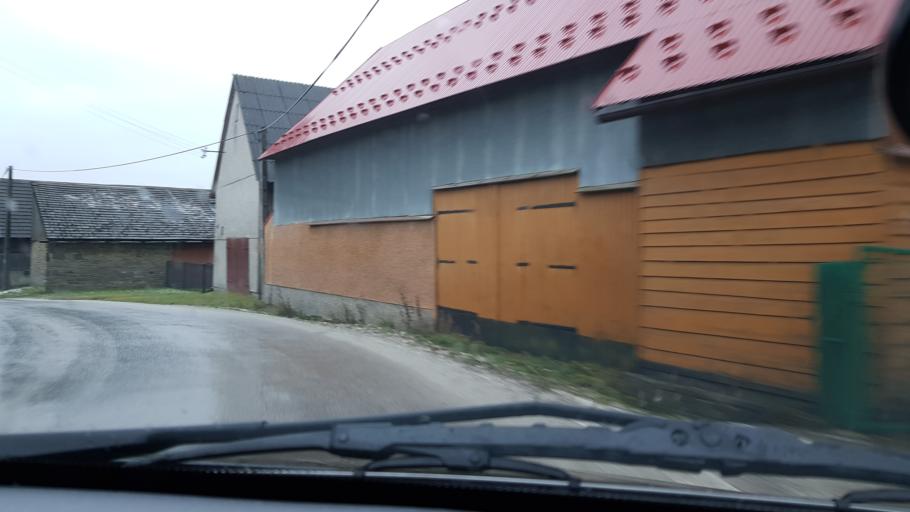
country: PL
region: Lesser Poland Voivodeship
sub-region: Powiat nowotarski
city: Sieniawa
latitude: 49.4882
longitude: 19.9042
